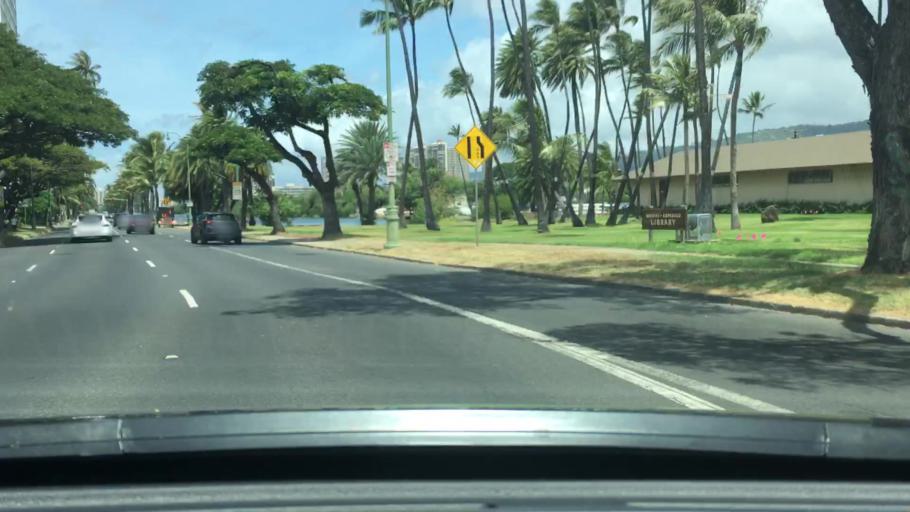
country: US
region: Hawaii
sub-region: Honolulu County
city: Honolulu
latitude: 21.2741
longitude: -157.8170
